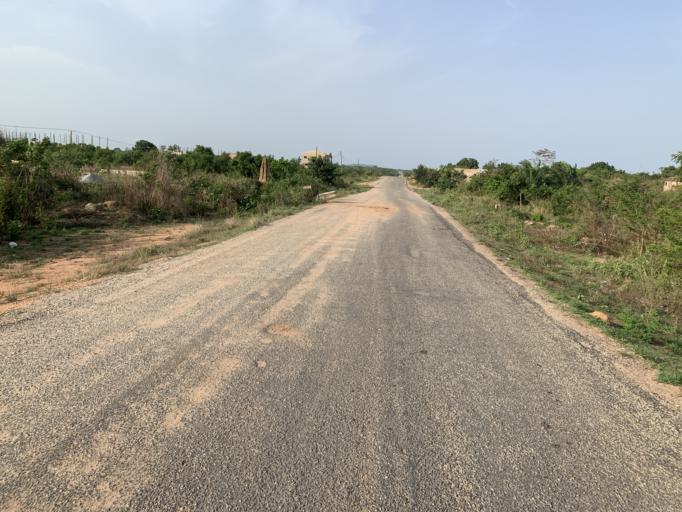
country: GH
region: Central
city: Winneba
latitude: 5.3788
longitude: -0.6101
